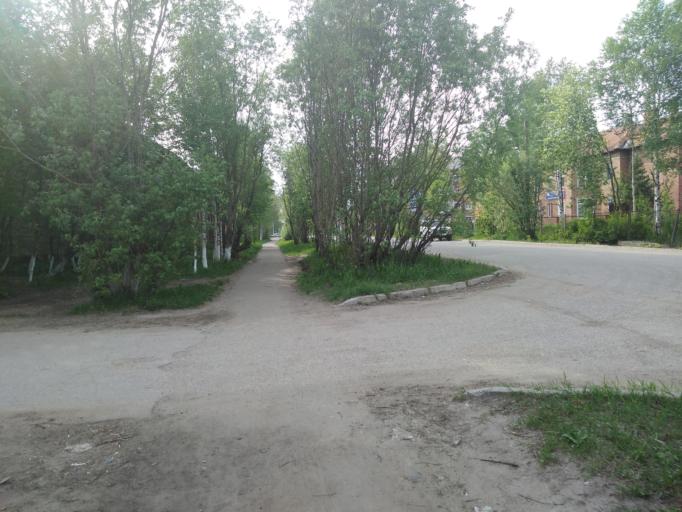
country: RU
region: Komi Republic
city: Pechora
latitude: 65.1458
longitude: 57.2237
